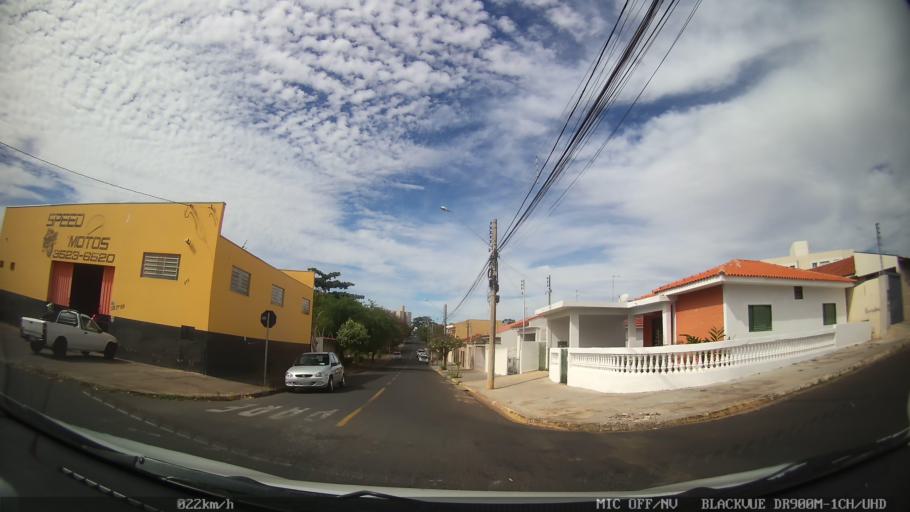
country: BR
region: Sao Paulo
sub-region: Catanduva
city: Catanduva
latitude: -21.1485
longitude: -48.9635
